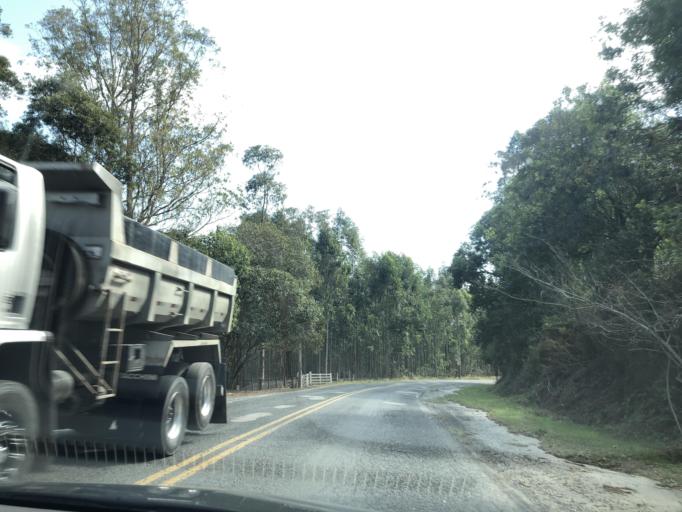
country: BR
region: Sao Paulo
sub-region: Pilar Do Sul
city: Pilar do Sul
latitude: -23.8154
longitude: -47.6315
